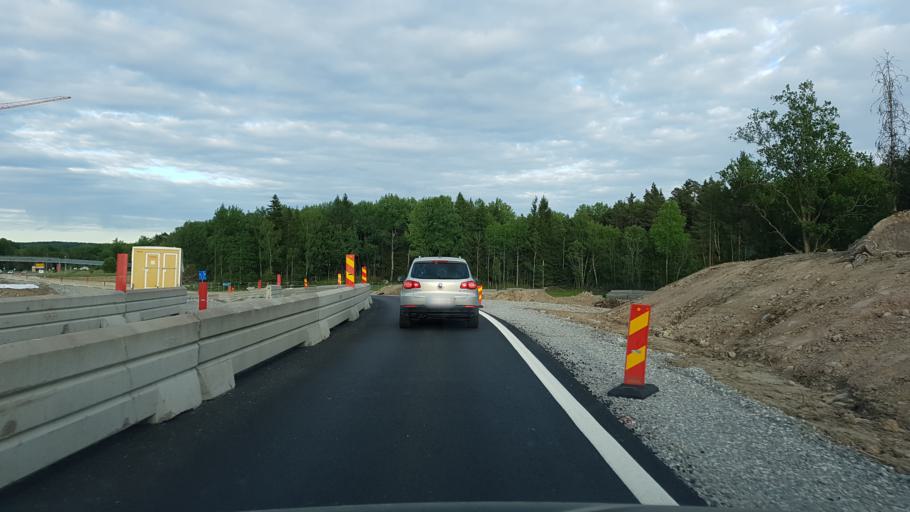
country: SE
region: Stockholm
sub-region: Upplands Vasby Kommun
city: Upplands Vaesby
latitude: 59.4747
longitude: 17.8777
